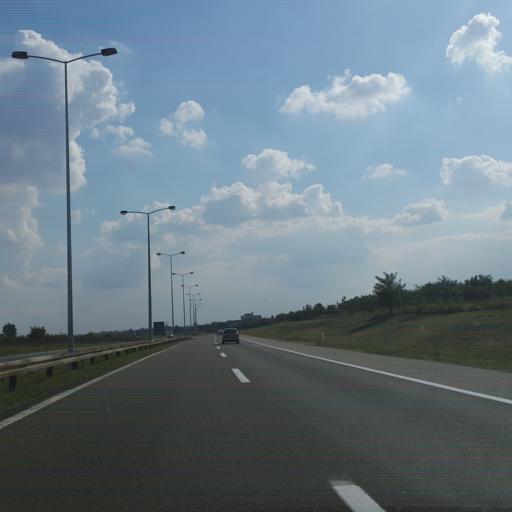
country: RS
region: Central Serbia
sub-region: Podunavski Okrug
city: Smederevo
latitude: 44.5734
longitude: 20.9804
